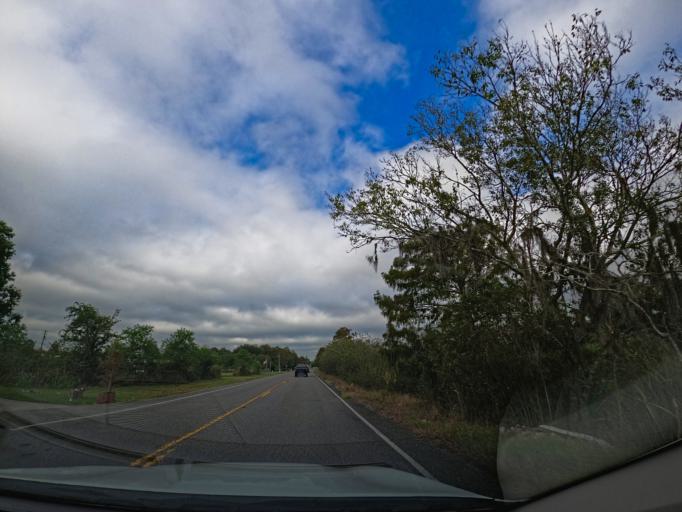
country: US
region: Louisiana
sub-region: Terrebonne Parish
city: Gray
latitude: 29.6170
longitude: -90.8986
